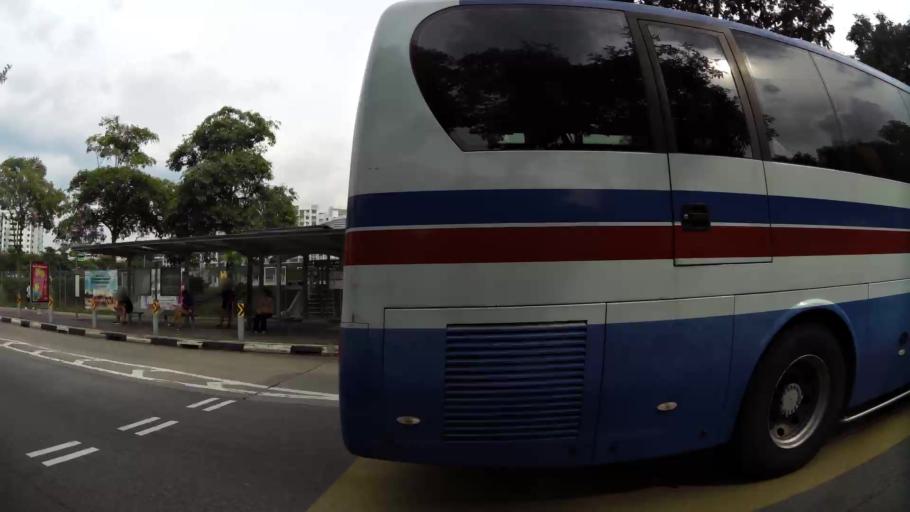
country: MY
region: Johor
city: Johor Bahru
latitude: 1.4309
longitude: 103.7875
